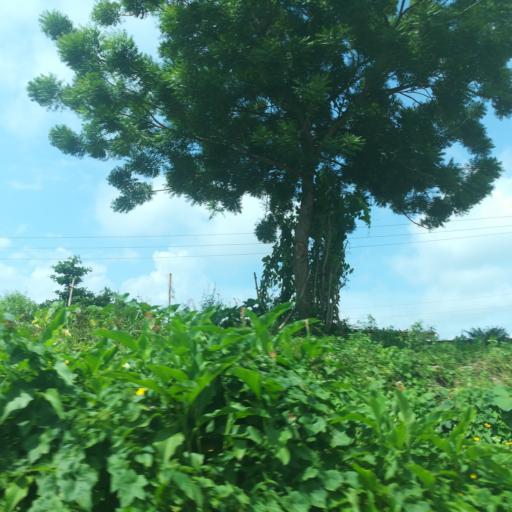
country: NG
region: Lagos
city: Ikorodu
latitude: 6.6669
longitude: 3.6741
